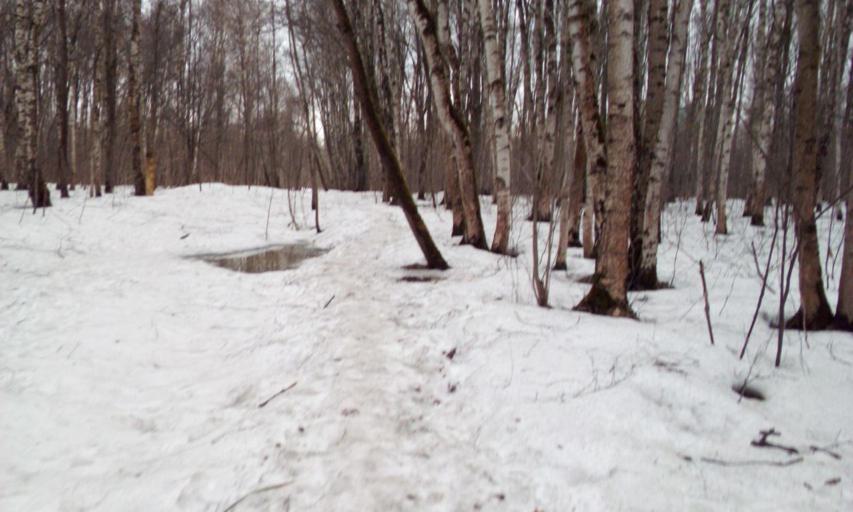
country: RU
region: Moskovskaya
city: Vostryakovo
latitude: 55.6532
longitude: 37.4561
